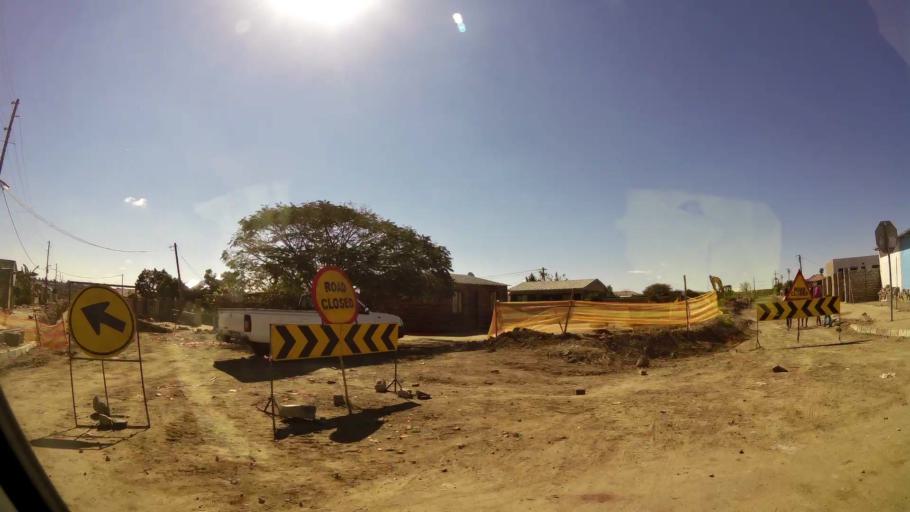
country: ZA
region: Limpopo
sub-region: Capricorn District Municipality
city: Polokwane
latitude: -23.8475
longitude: 29.4123
